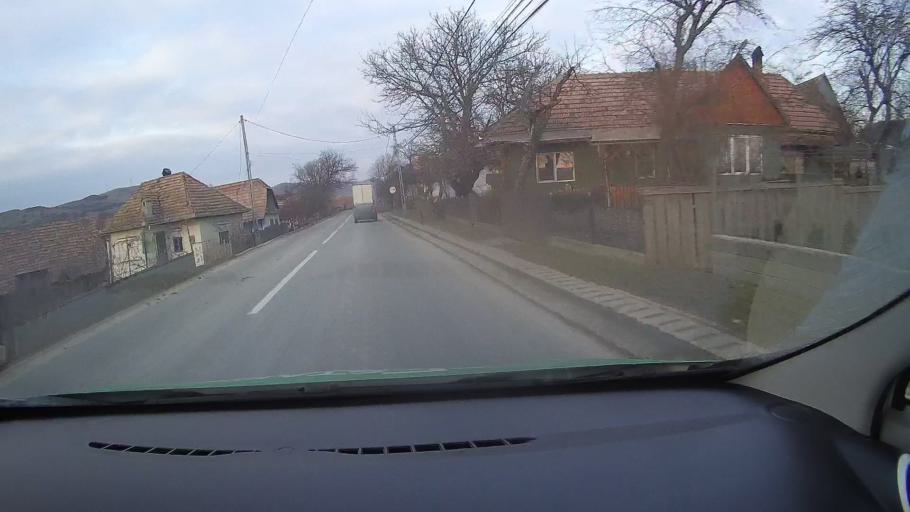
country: RO
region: Harghita
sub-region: Comuna Simonesti
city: Simonesti
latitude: 46.3420
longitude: 25.1146
